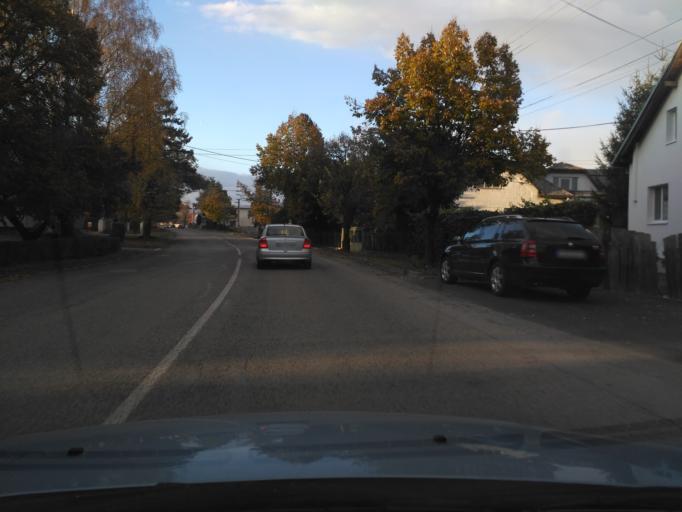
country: SK
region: Kosicky
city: Trebisov
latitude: 48.6503
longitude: 21.6786
